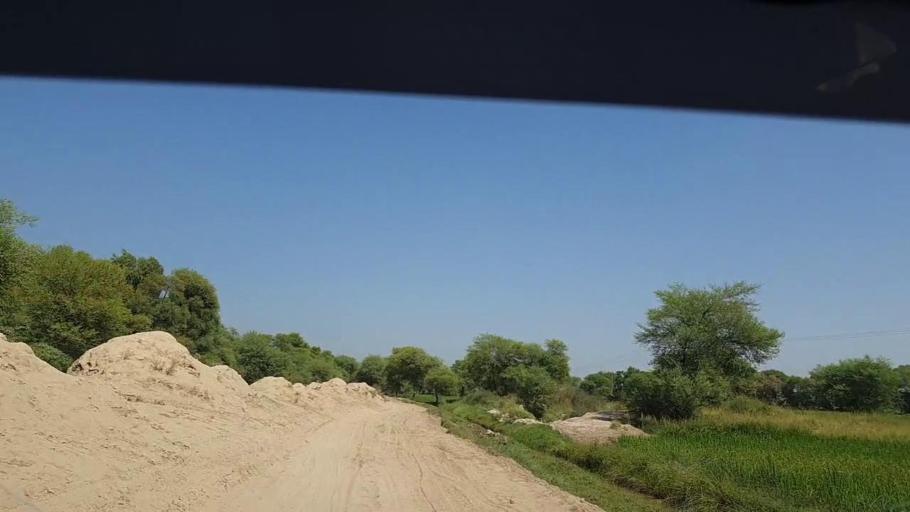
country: PK
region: Sindh
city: Tangwani
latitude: 28.2892
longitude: 69.0556
